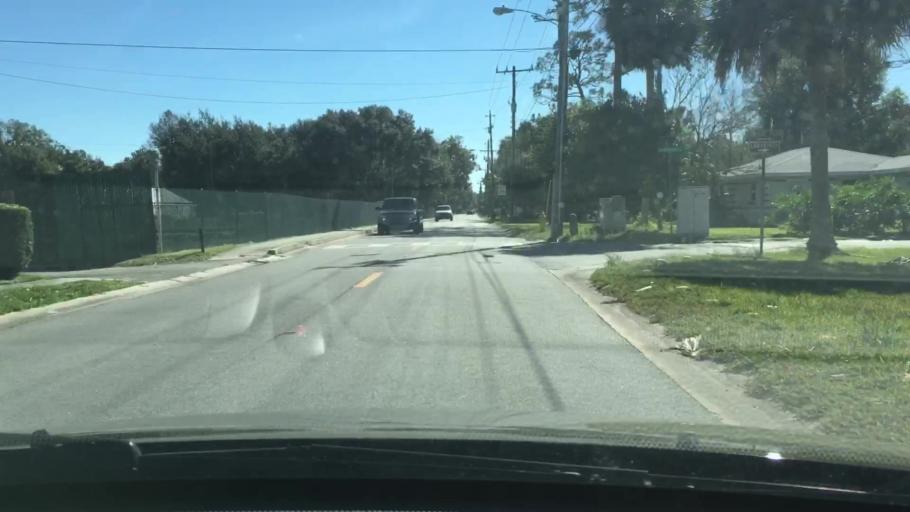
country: US
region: Florida
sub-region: Volusia County
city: Ormond Beach
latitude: 29.2755
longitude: -81.0658
